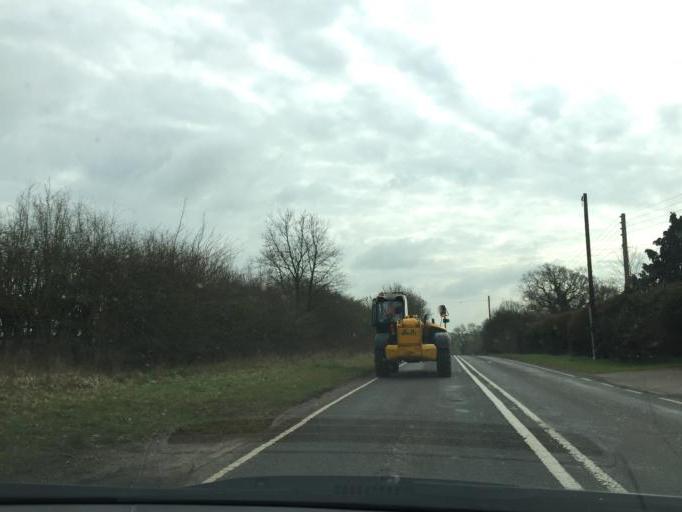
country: GB
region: England
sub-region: Warwickshire
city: Henley in Arden
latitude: 52.2890
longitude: -1.7961
